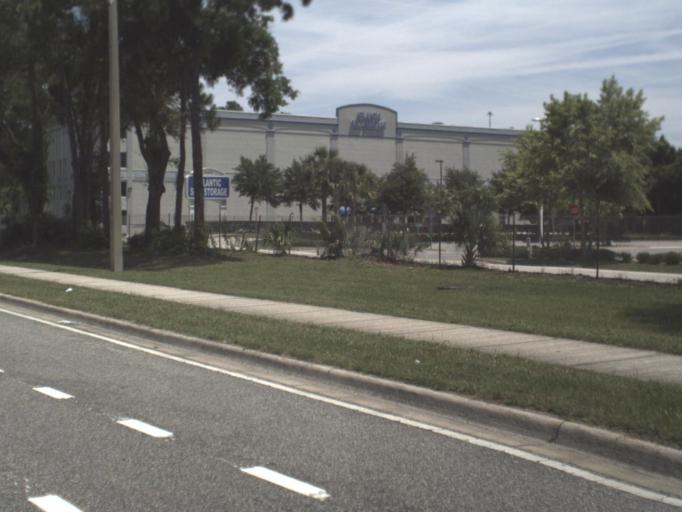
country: US
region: Florida
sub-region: Saint Johns County
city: Fruit Cove
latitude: 30.1785
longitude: -81.6278
